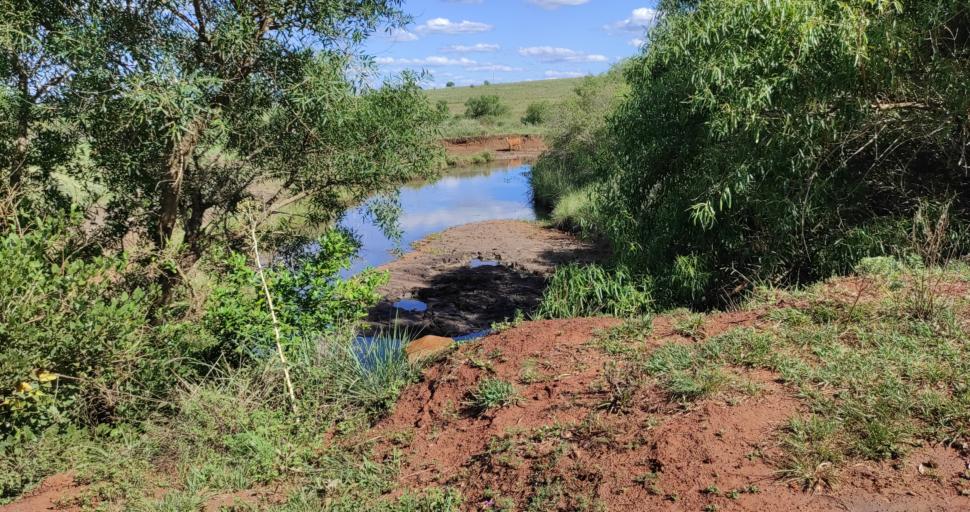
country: PY
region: Itapua
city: San Juan del Parana
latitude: -27.4455
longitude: -56.0632
